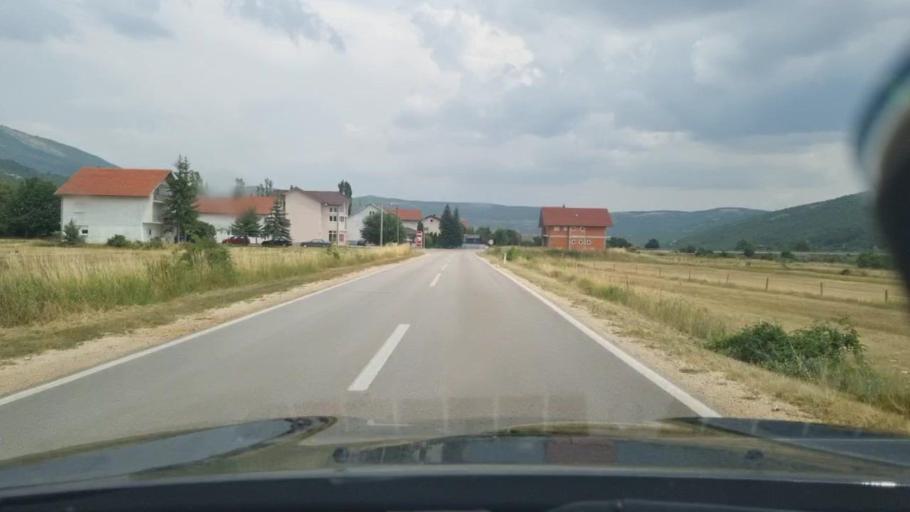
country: BA
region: Federation of Bosnia and Herzegovina
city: Podhum
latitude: 43.6882
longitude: 17.0775
